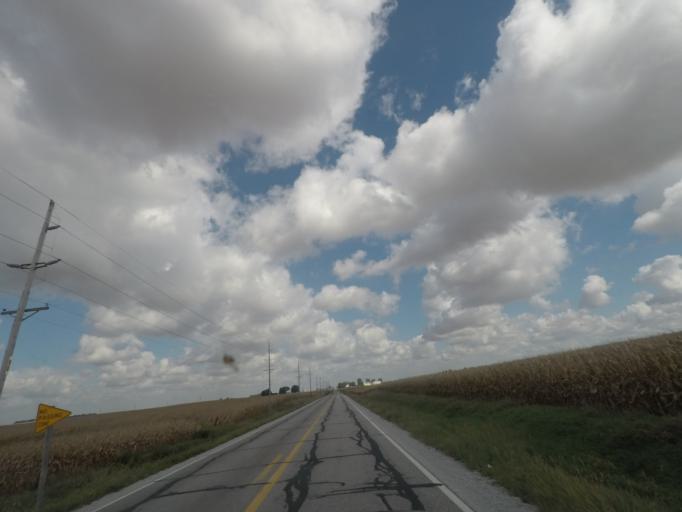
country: US
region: Iowa
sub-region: Story County
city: Nevada
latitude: 42.0164
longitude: -93.4057
